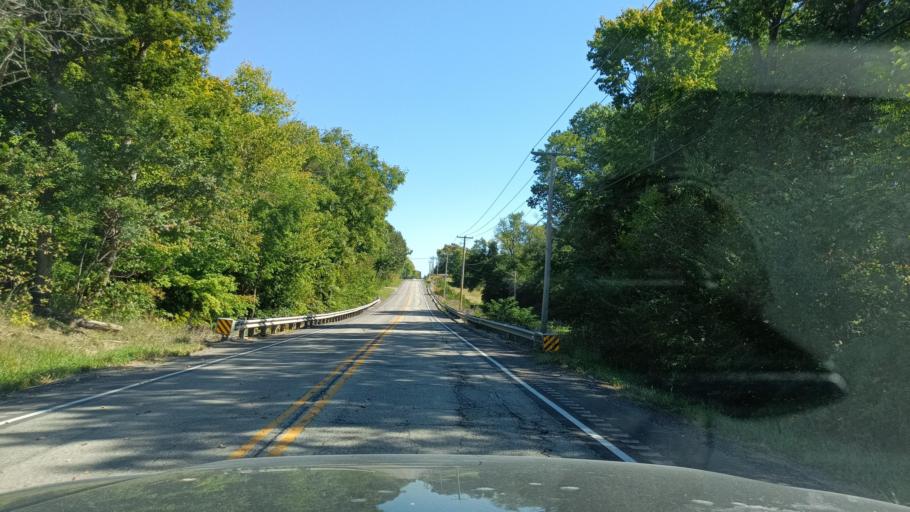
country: US
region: Illinois
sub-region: McLean County
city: Danvers
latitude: 40.6170
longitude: -89.2182
